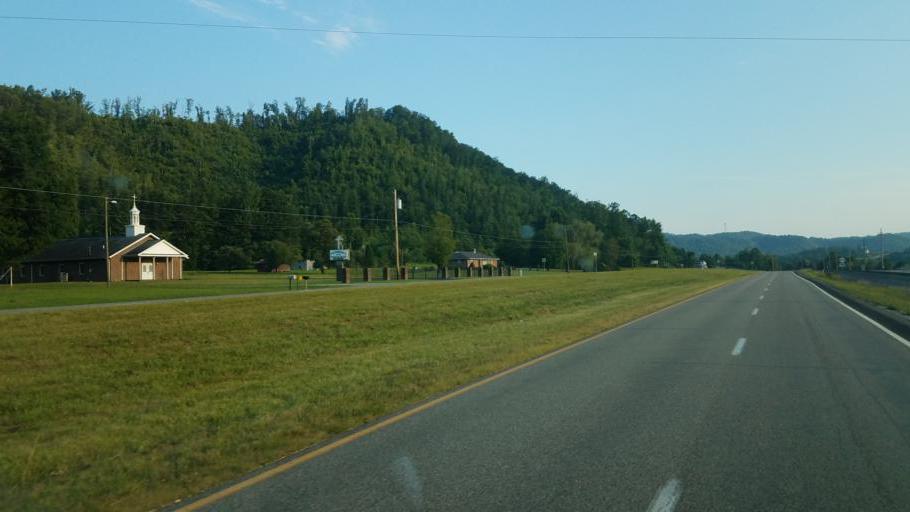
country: US
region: Virginia
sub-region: Lee County
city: Dryden
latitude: 36.7300
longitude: -82.7971
